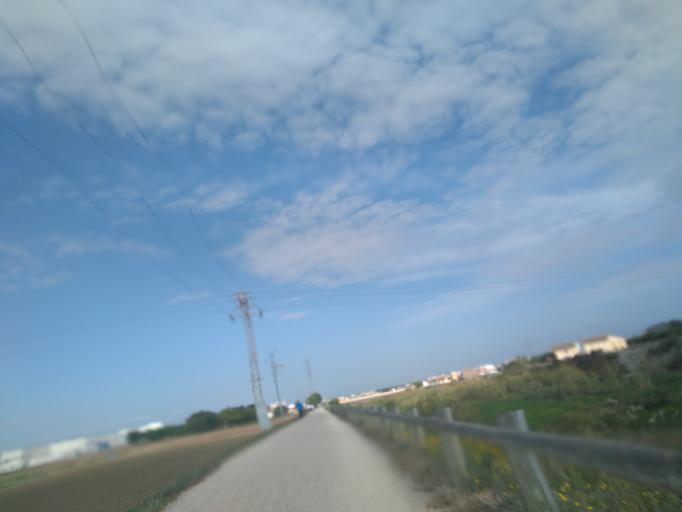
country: ES
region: Valencia
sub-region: Provincia de Valencia
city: Alboraya
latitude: 39.5037
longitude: -0.3391
